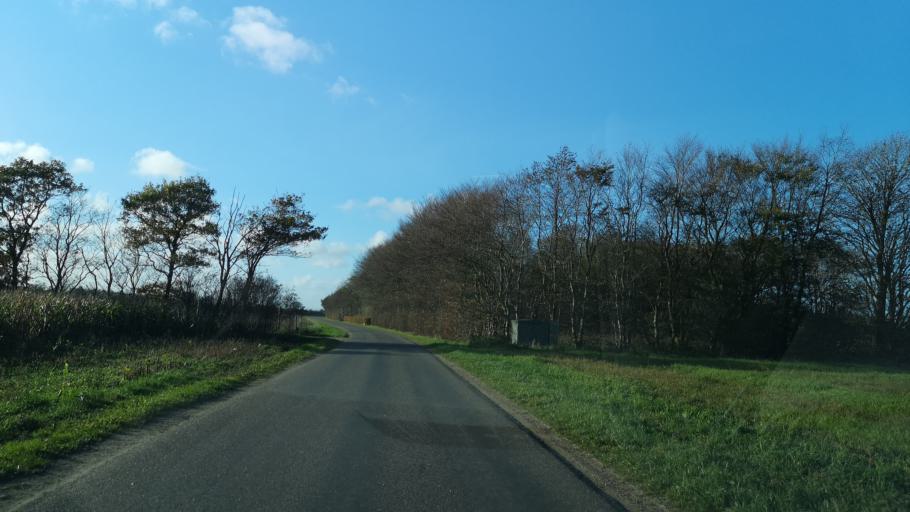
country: DK
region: Central Jutland
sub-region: Ringkobing-Skjern Kommune
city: Tarm
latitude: 55.8291
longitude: 8.3872
